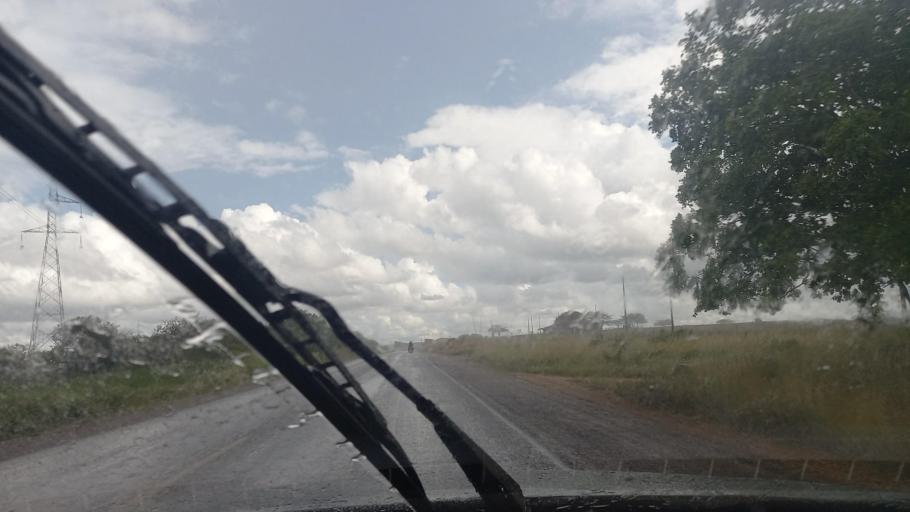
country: BR
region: Pernambuco
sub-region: Lajedo
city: Lajedo
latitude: -8.5756
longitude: -36.2850
